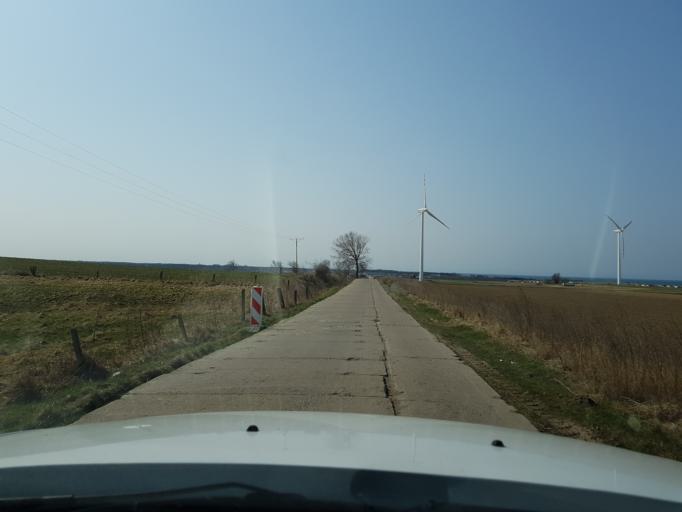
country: PL
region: West Pomeranian Voivodeship
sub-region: Powiat slawienski
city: Darlowo
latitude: 54.4446
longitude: 16.4262
